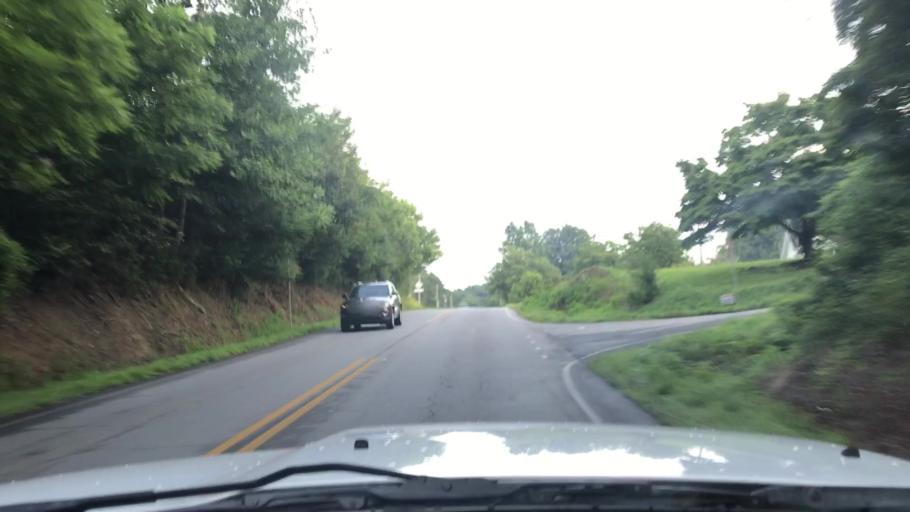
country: US
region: Georgia
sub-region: Fannin County
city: Blue Ridge
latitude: 34.9029
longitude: -84.2662
